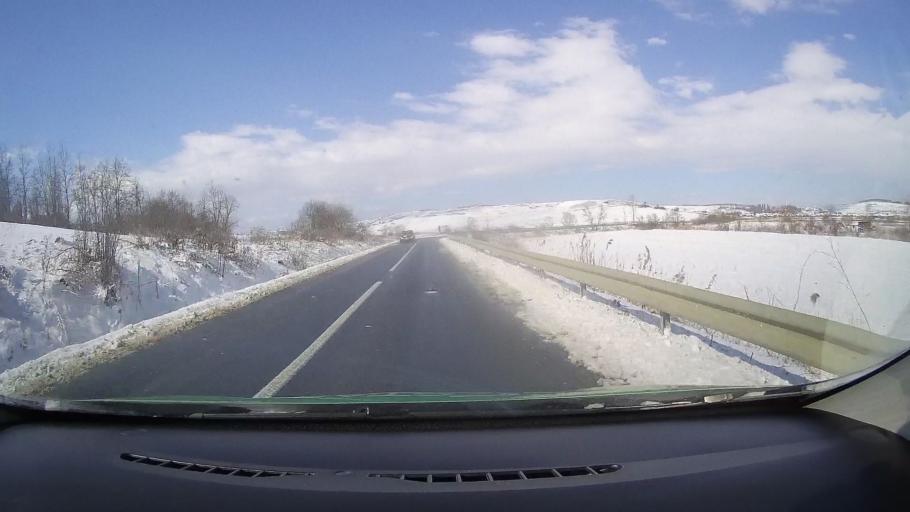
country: RO
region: Sibiu
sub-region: Comuna Nocrich
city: Nocrich
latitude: 45.9097
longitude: 24.4612
